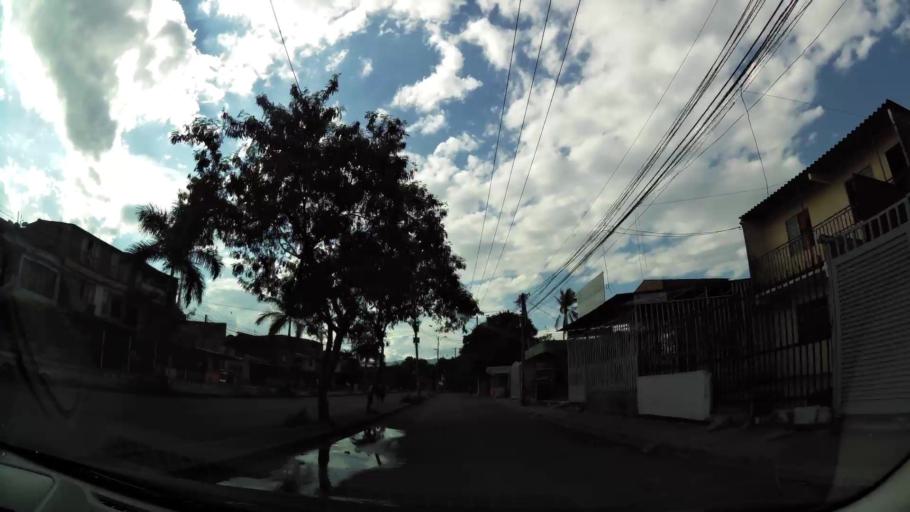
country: CO
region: Valle del Cauca
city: Cali
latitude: 3.4154
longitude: -76.4938
